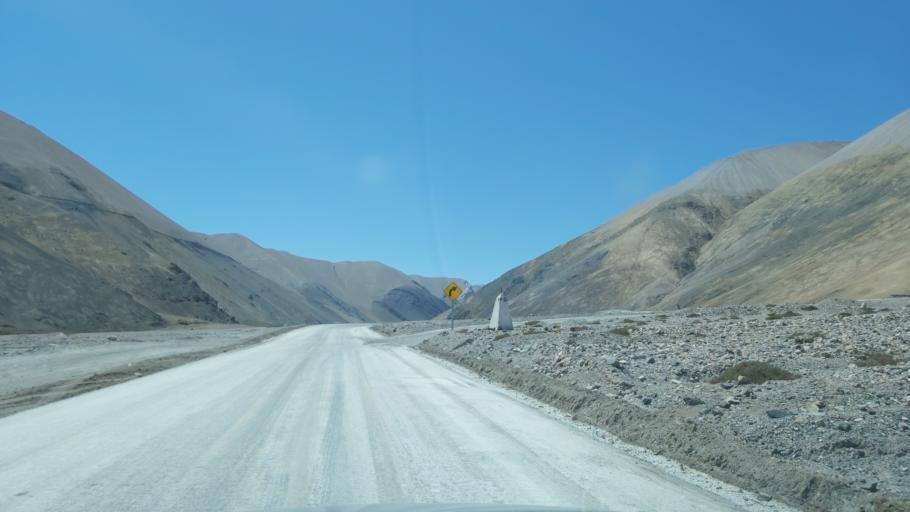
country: CL
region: Atacama
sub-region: Provincia de Chanaral
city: Diego de Almagro
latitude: -26.3963
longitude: -69.5143
